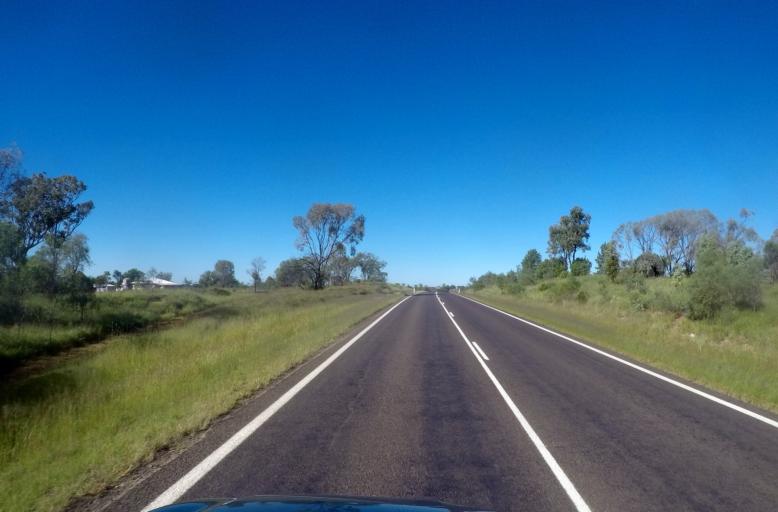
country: AU
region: Queensland
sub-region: Maranoa
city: Roma
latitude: -26.4790
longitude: 148.7982
